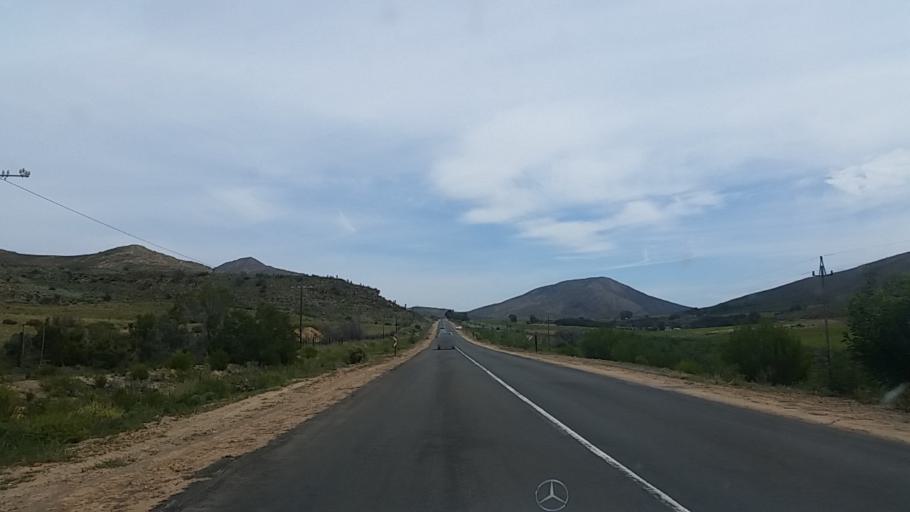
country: ZA
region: Western Cape
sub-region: Eden District Municipality
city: George
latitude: -33.8202
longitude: 22.3743
